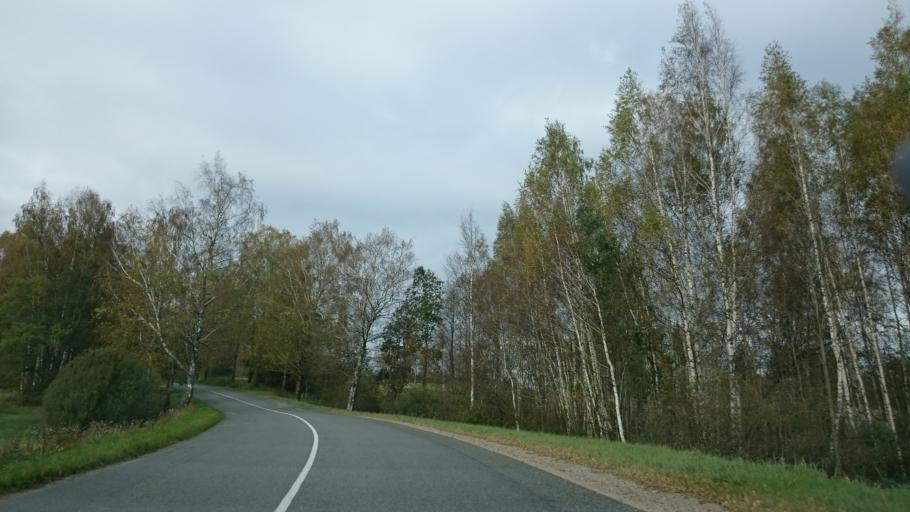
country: LV
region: Amatas Novads
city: Drabesi
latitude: 57.2764
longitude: 25.2700
